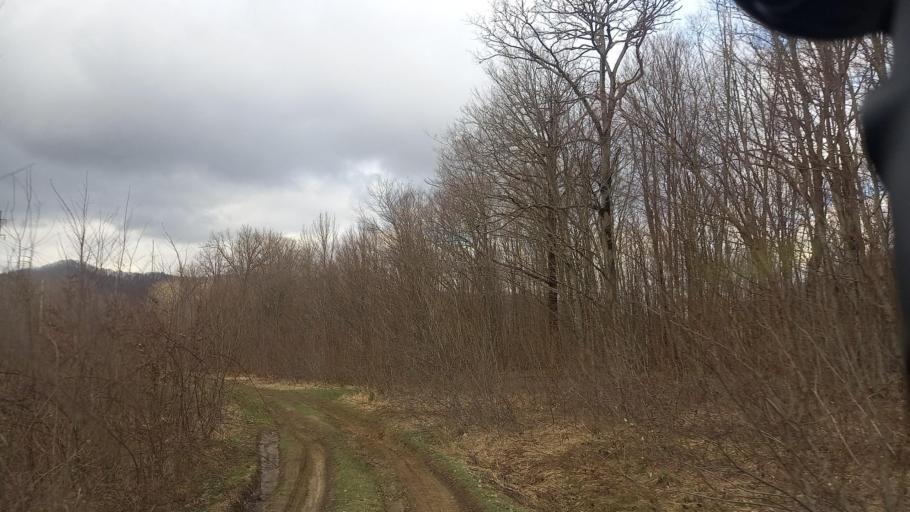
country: RU
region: Krasnodarskiy
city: Dzhubga
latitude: 44.5268
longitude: 38.7733
